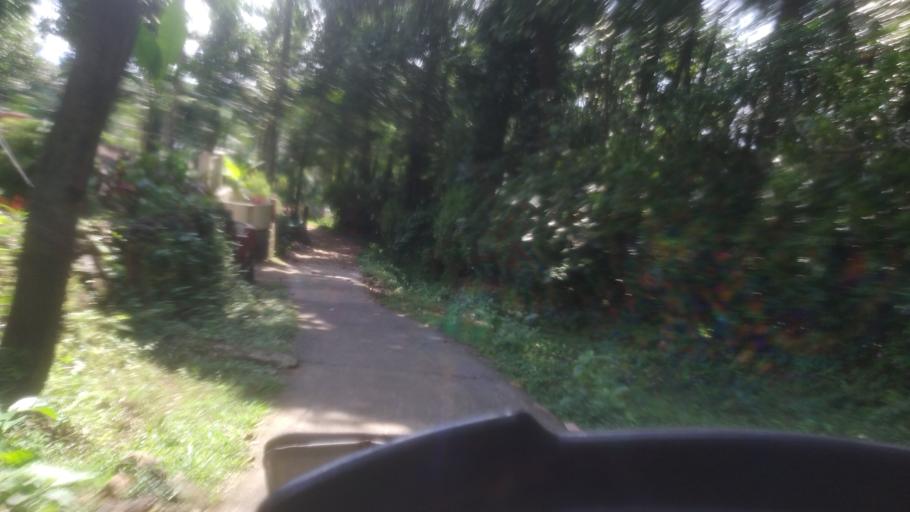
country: IN
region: Kerala
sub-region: Idukki
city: Idukki
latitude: 9.9616
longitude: 76.8252
